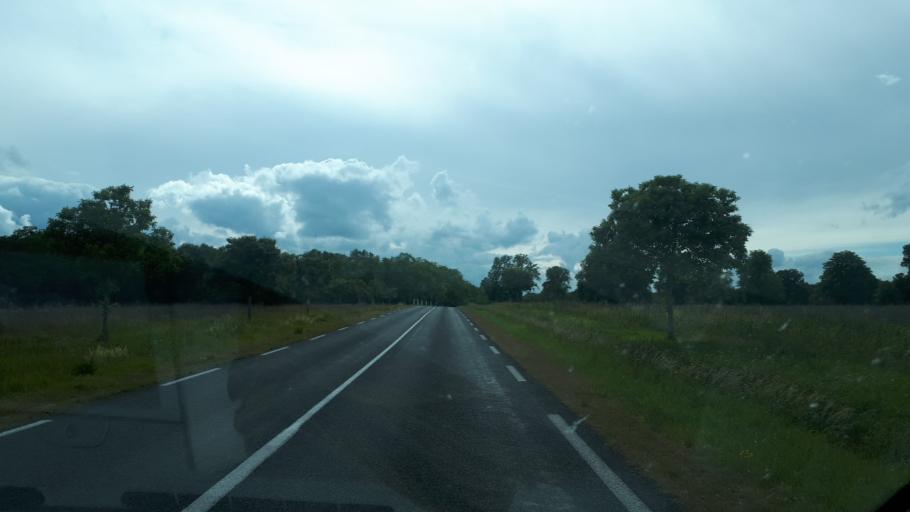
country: FR
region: Centre
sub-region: Departement du Cher
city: Mehun-sur-Yevre
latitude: 47.0774
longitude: 2.1773
